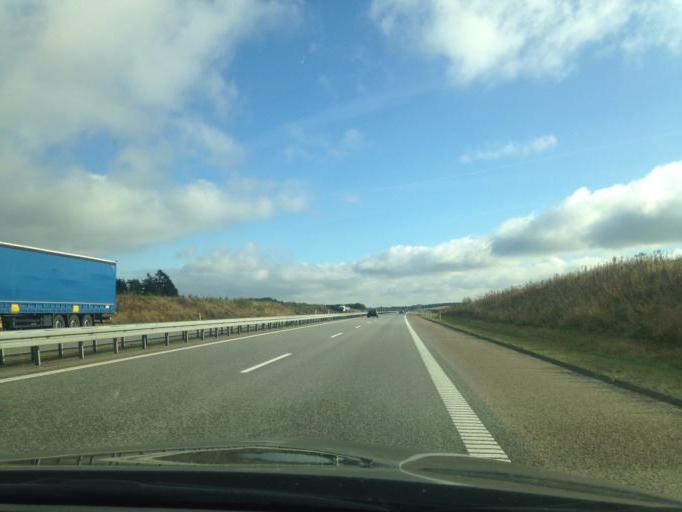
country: DK
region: South Denmark
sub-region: Vejle Kommune
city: Jelling
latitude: 55.8362
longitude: 9.3981
